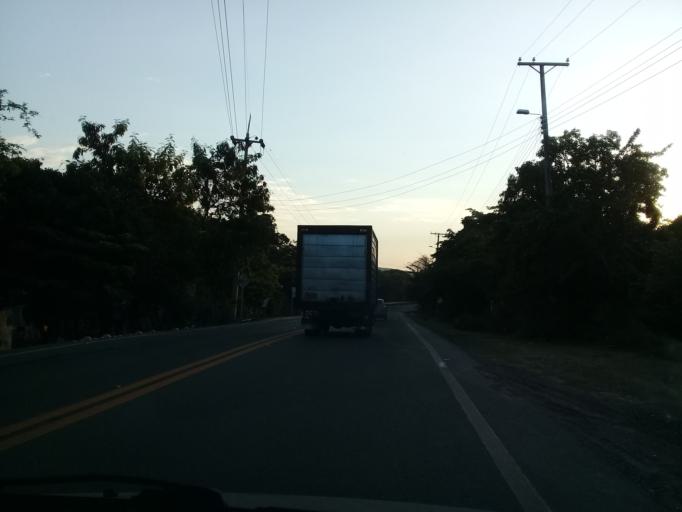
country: CO
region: Cundinamarca
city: Agua de Dios
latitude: 4.3980
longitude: -74.7348
